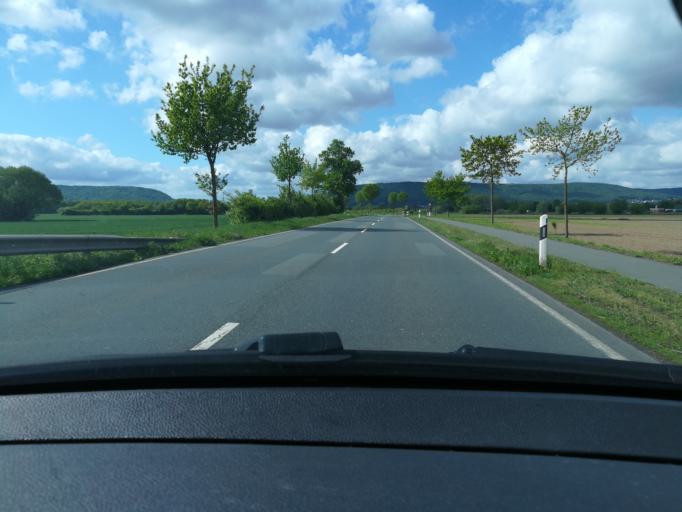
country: DE
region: North Rhine-Westphalia
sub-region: Regierungsbezirk Detmold
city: Minden
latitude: 52.2803
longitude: 8.9284
